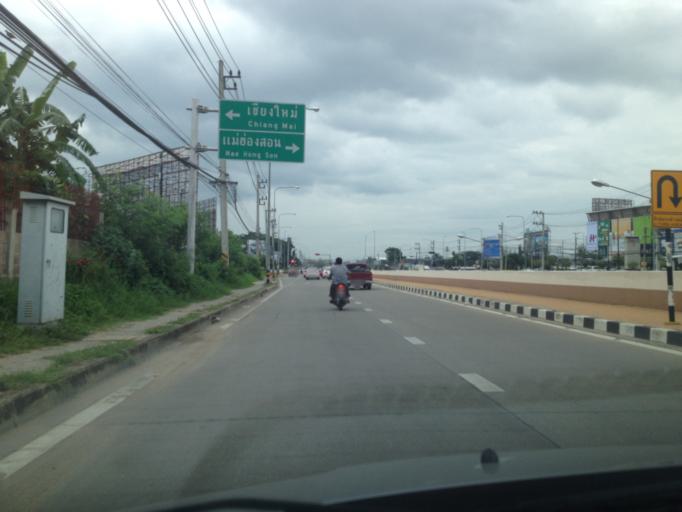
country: TH
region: Chiang Mai
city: Chiang Mai
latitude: 18.7443
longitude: 98.9580
